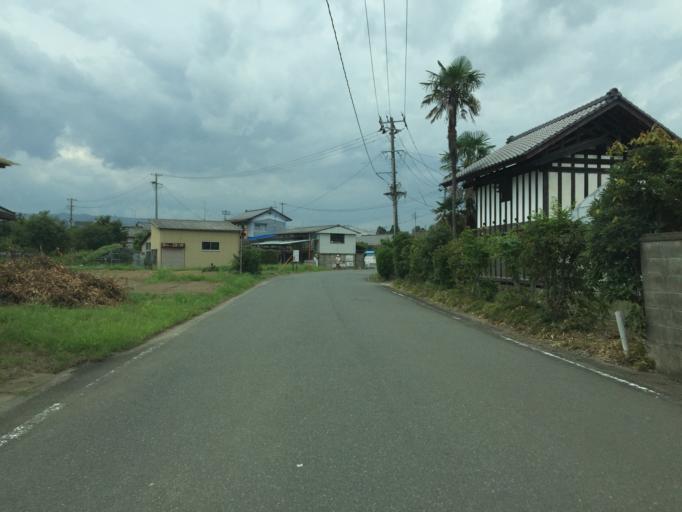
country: JP
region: Miyagi
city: Marumori
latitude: 37.7938
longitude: 140.9350
